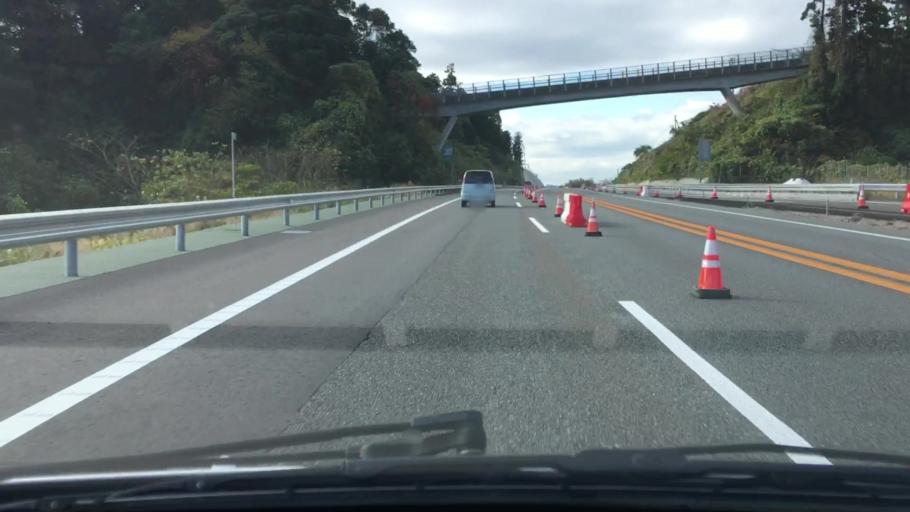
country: JP
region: Chiba
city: Kimitsu
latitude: 35.2728
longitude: 139.9177
